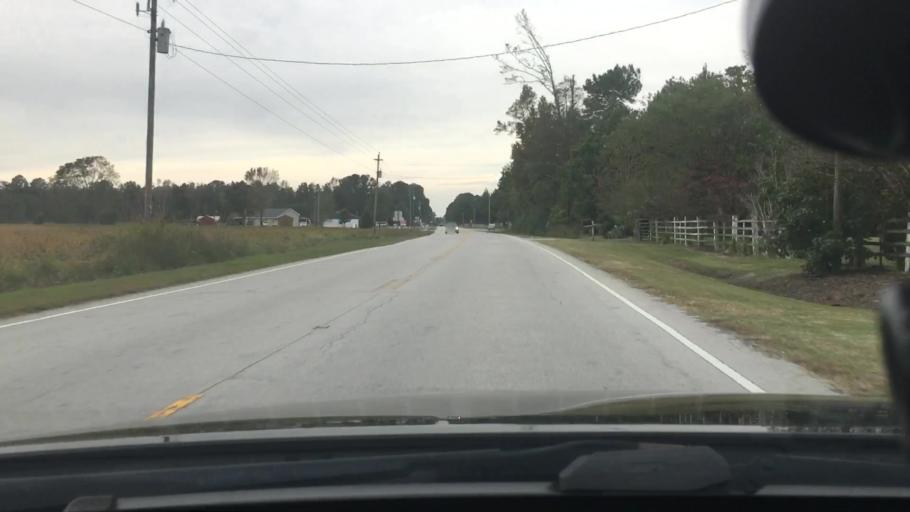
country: US
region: North Carolina
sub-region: Craven County
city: Vanceboro
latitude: 35.3395
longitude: -77.1764
